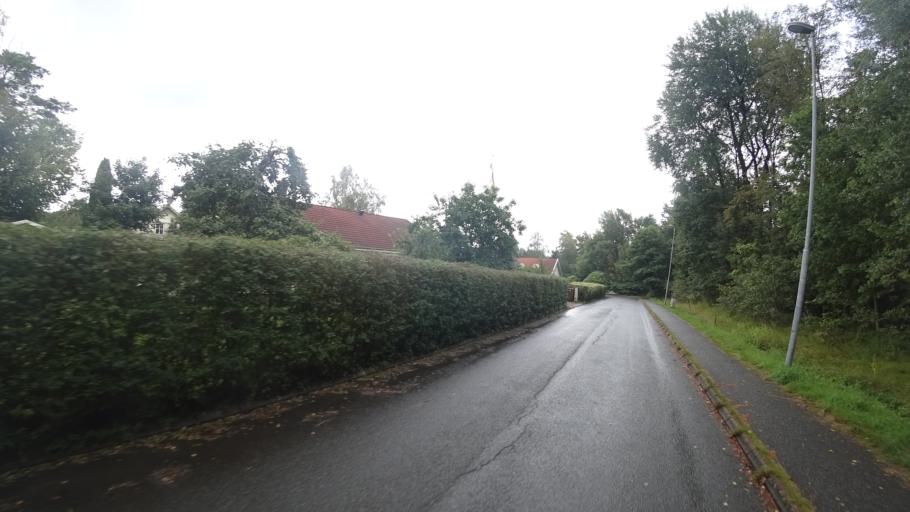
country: SE
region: Vaestra Goetaland
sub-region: Partille Kommun
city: Furulund
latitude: 57.7011
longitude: 12.1376
